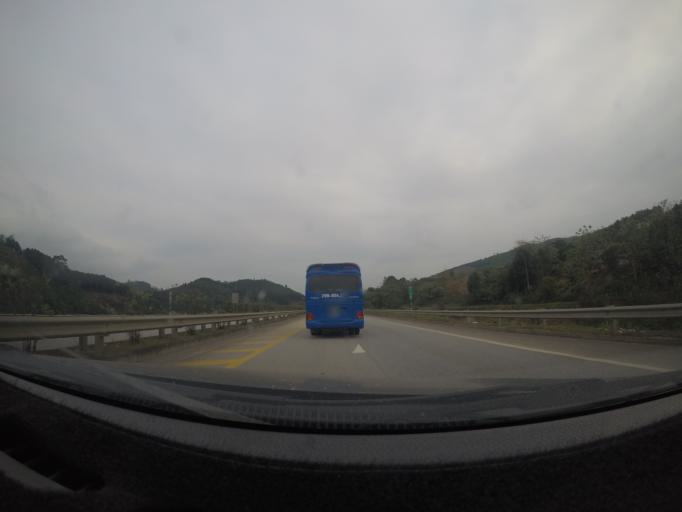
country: VN
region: Yen Bai
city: Thi Tran Yen The
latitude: 21.9206
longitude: 104.6108
